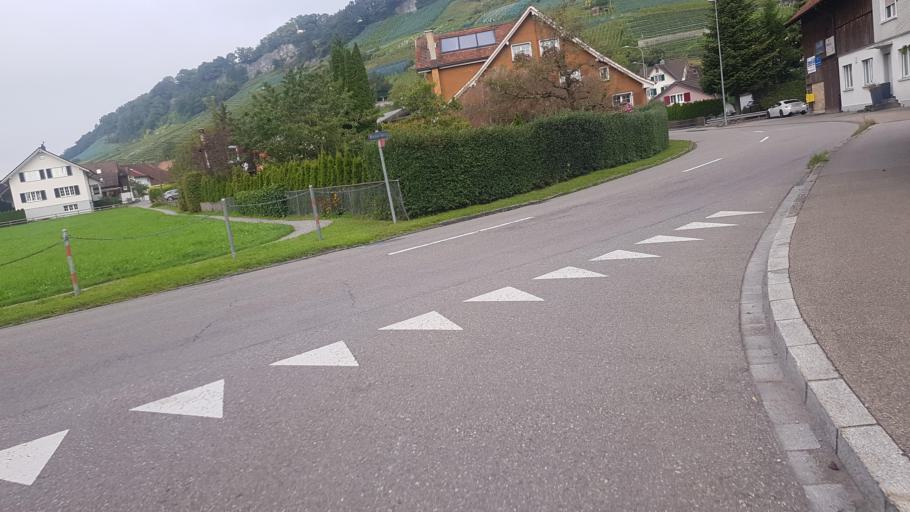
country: CH
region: Saint Gallen
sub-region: Wahlkreis Rheintal
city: Rheineck
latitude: 47.4696
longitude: 9.5757
